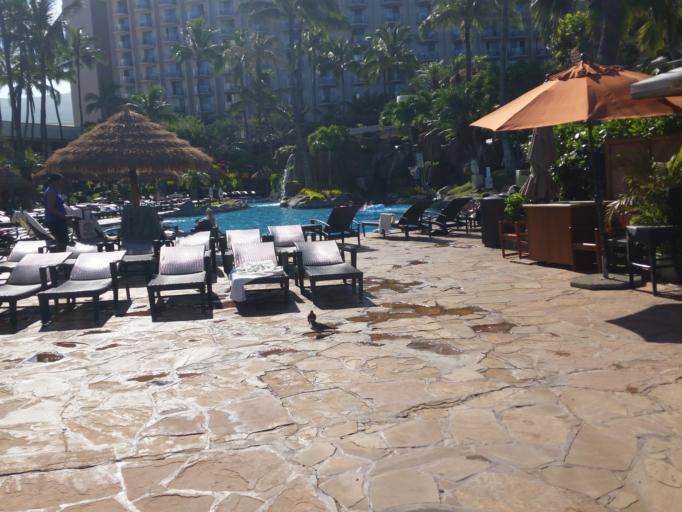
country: US
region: Hawaii
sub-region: Maui County
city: Ka'anapali
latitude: 20.9203
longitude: -156.6960
